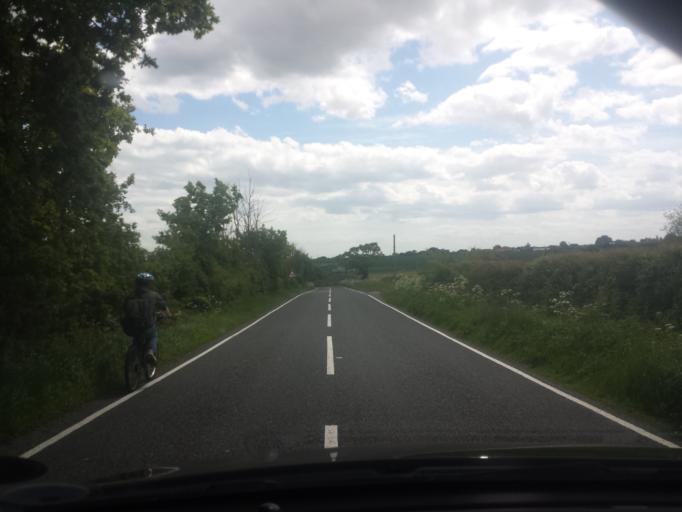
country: GB
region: England
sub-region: Essex
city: Little Clacton
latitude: 51.8331
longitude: 1.1556
